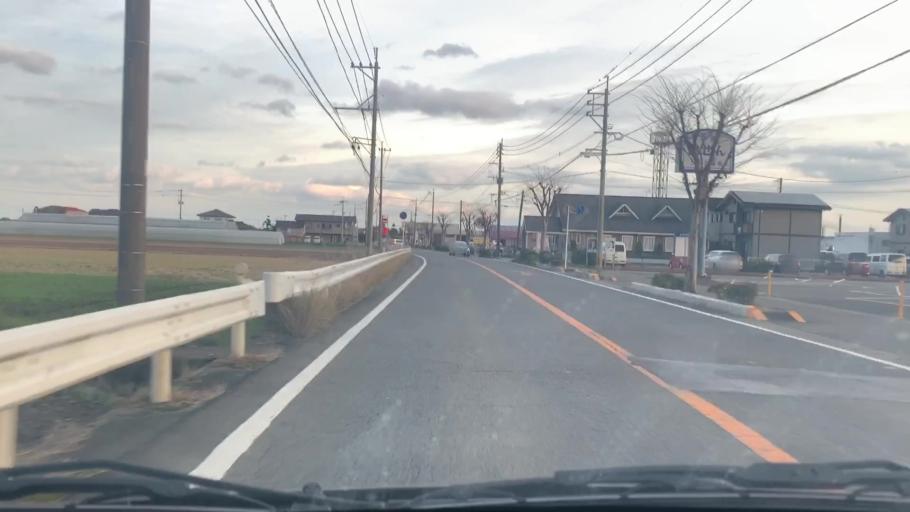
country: JP
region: Saga Prefecture
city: Kashima
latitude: 33.1253
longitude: 130.0694
